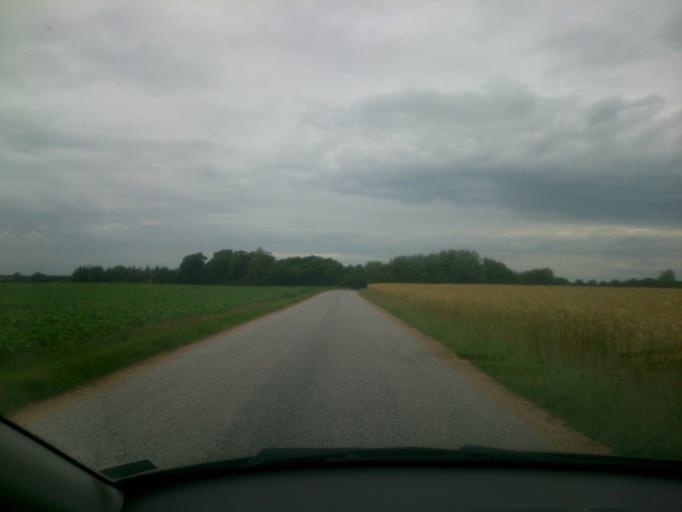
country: DK
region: South Denmark
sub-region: Varde Kommune
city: Varde
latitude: 55.5600
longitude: 8.4226
